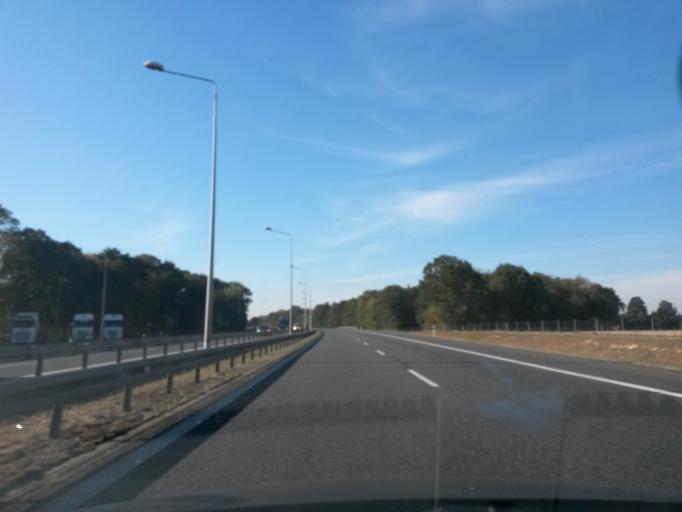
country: PL
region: Opole Voivodeship
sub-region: Powiat brzeski
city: Grodkow
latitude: 50.7655
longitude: 17.4124
